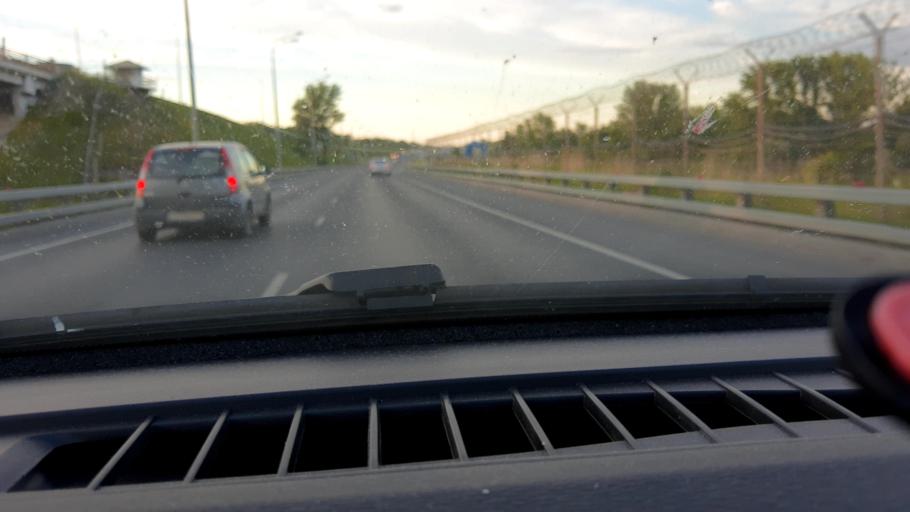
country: RU
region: Nizjnij Novgorod
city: Neklyudovo
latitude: 56.3616
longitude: 43.9322
